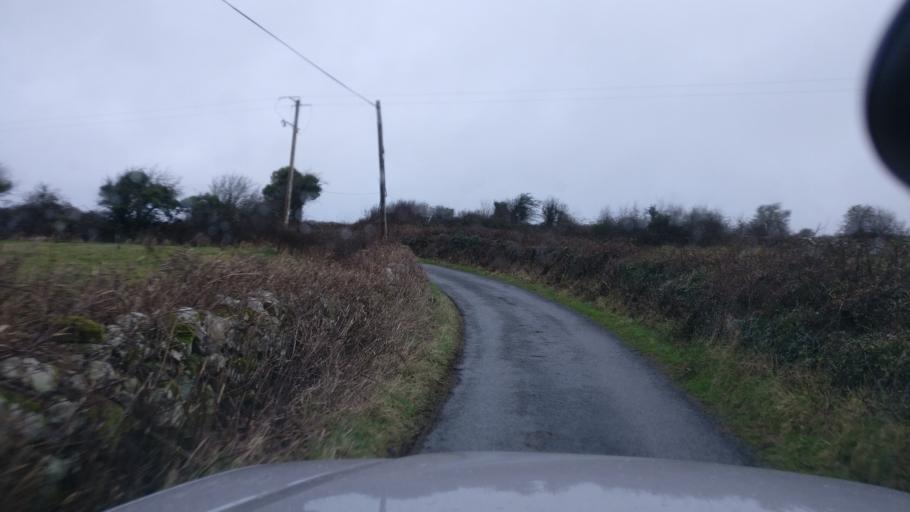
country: IE
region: Connaught
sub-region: County Galway
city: Loughrea
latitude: 53.1596
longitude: -8.6105
